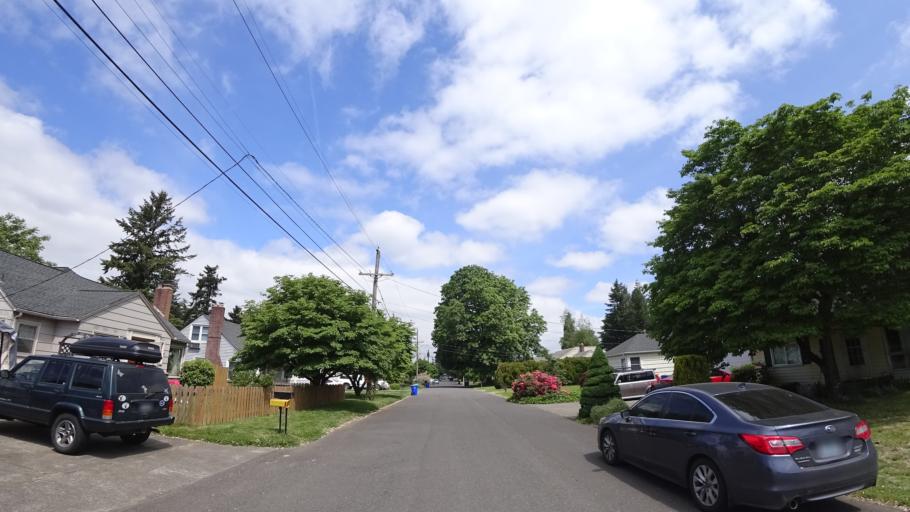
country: US
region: Oregon
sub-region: Multnomah County
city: Gresham
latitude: 45.5021
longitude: -122.4937
